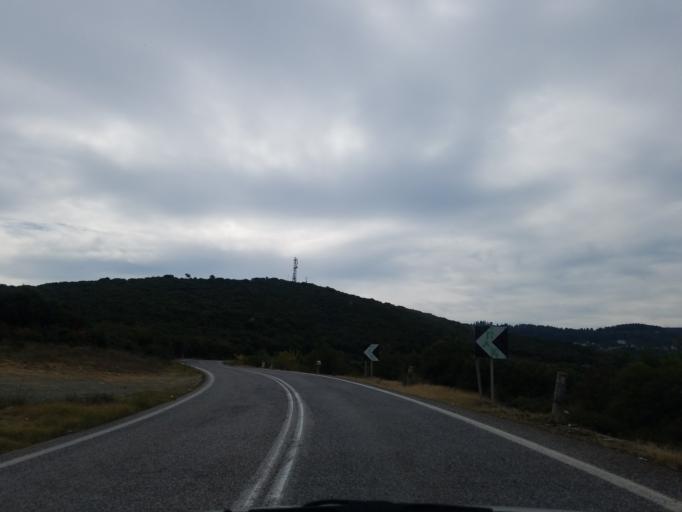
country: GR
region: Central Greece
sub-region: Nomos Fthiotidos
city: Domokos
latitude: 39.1390
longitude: 22.3099
